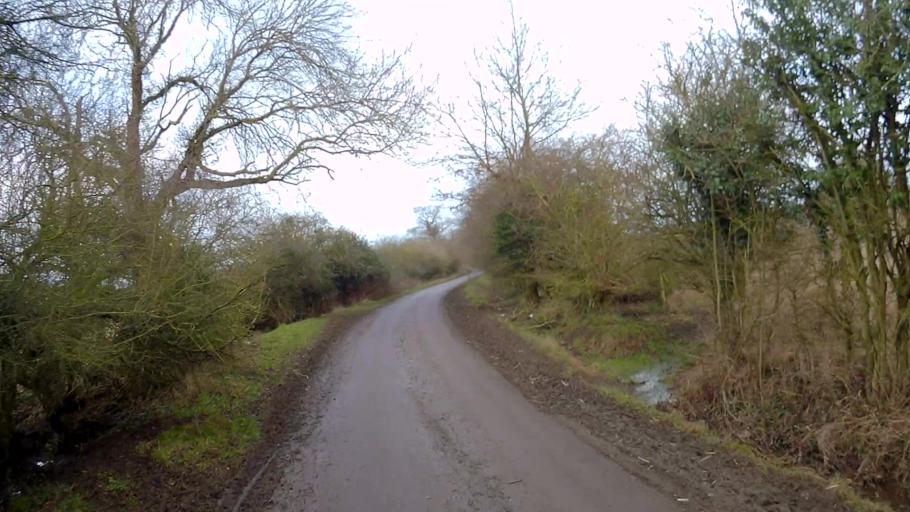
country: GB
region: England
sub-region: Lincolnshire
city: Bourne
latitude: 52.8138
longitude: -0.4364
